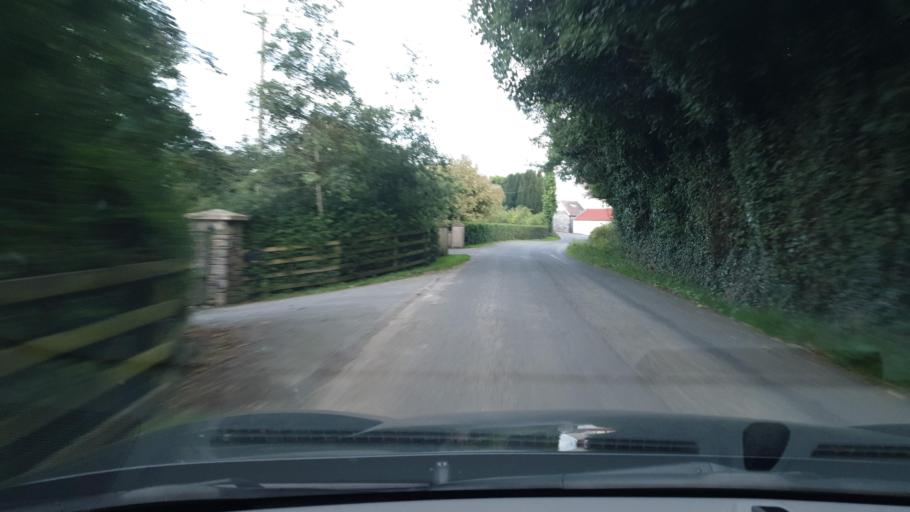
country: IE
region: Leinster
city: Balrothery
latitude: 53.5655
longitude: -6.1965
